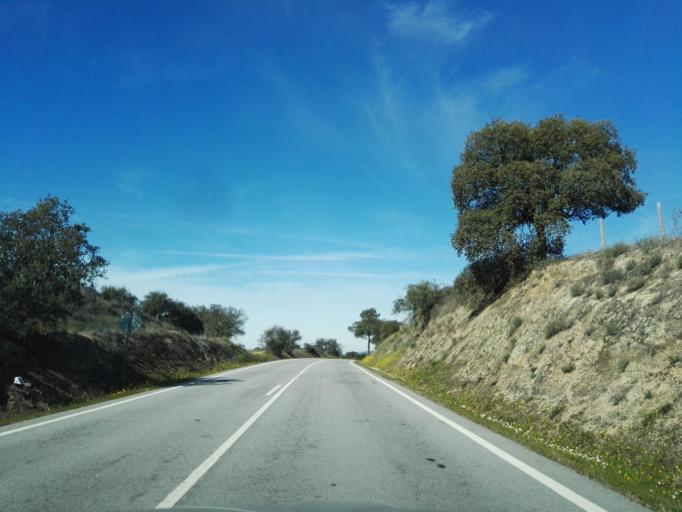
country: PT
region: Portalegre
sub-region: Arronches
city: Arronches
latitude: 39.0789
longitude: -7.2802
